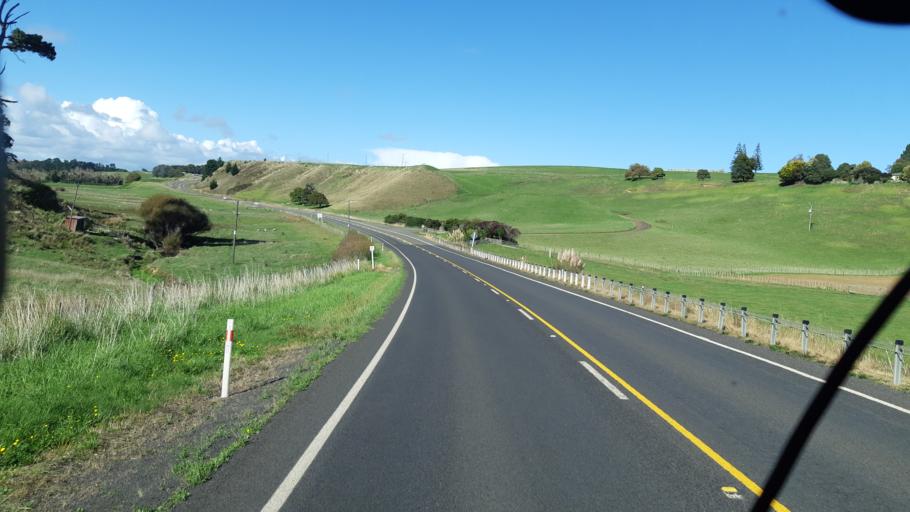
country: NZ
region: Manawatu-Wanganui
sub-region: Wanganui District
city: Wanganui
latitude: -39.9661
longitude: 175.1013
